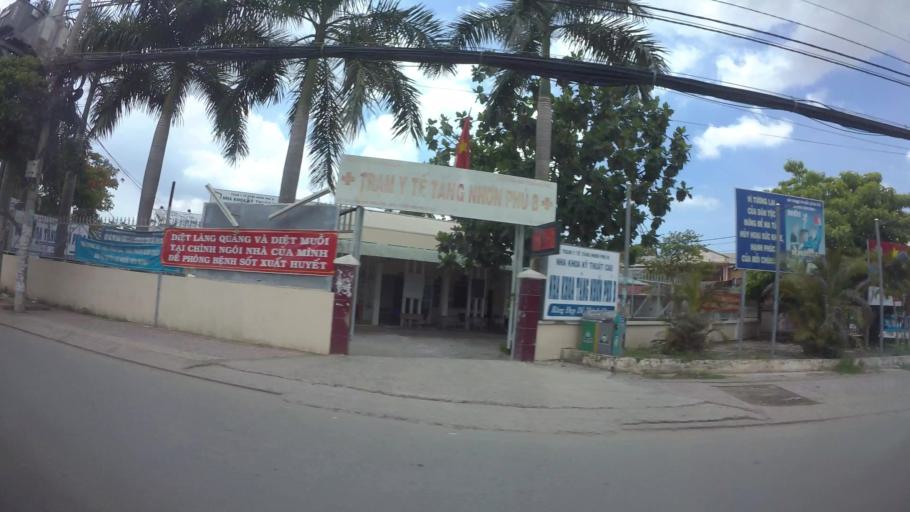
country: VN
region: Ho Chi Minh City
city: Quan Chin
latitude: 10.8333
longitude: 106.7836
